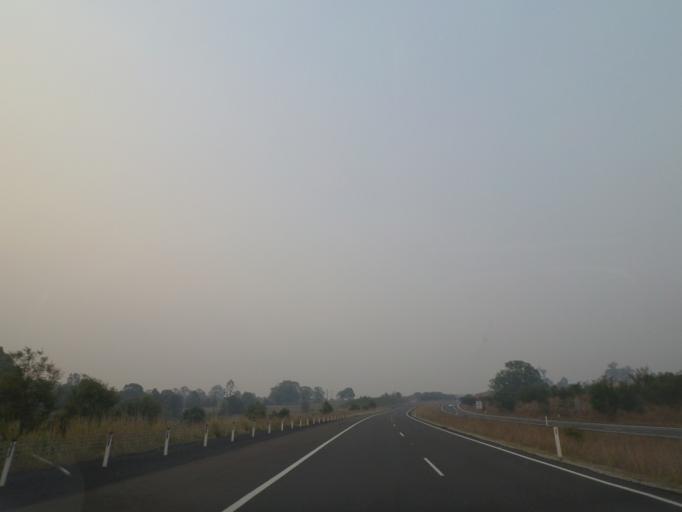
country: AU
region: New South Wales
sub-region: Nambucca Shire
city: Macksville
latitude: -30.7615
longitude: 152.9042
